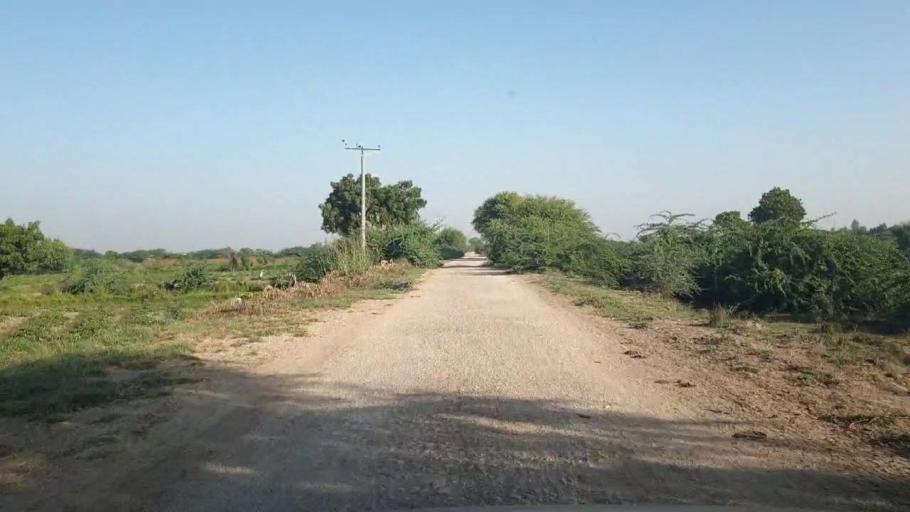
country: PK
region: Sindh
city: Badin
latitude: 24.6926
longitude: 68.8160
